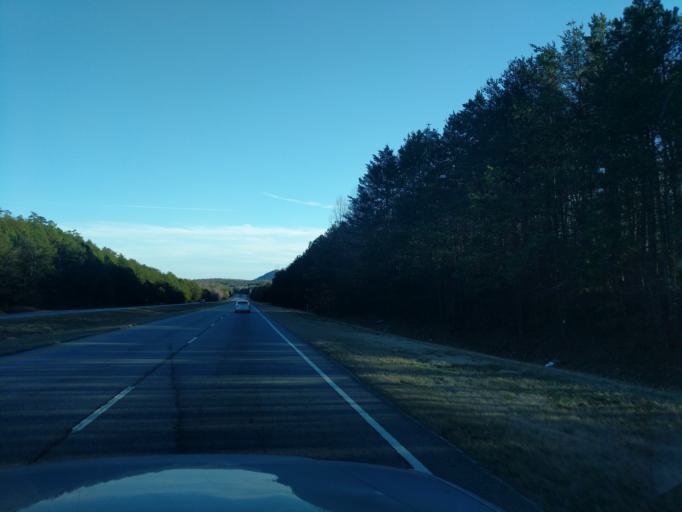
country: US
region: Georgia
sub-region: Stephens County
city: Toccoa
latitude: 34.5786
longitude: -83.4074
